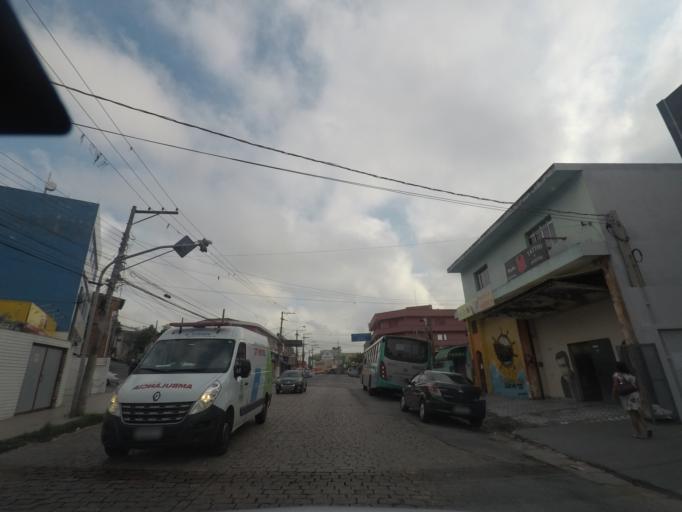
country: BR
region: Sao Paulo
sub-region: Osasco
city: Osasco
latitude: -23.5720
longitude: -46.7790
